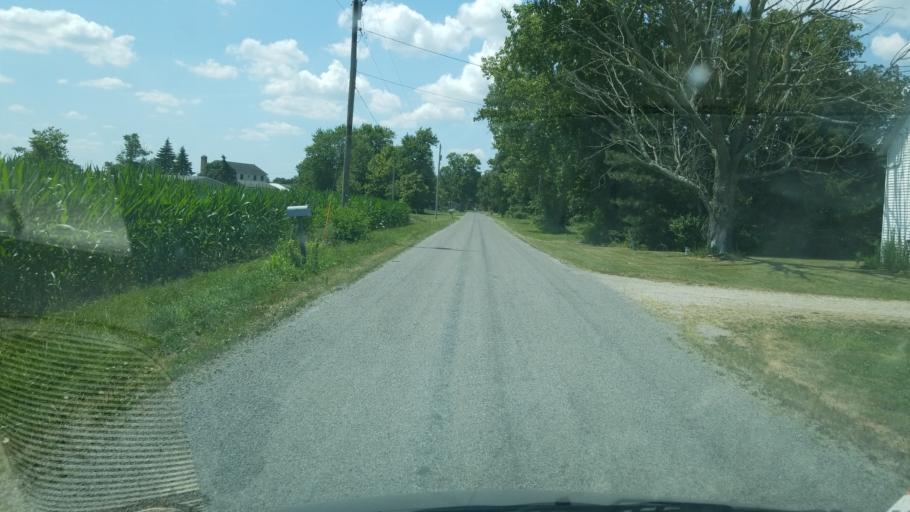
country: US
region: Ohio
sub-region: Champaign County
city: Mechanicsburg
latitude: 40.0783
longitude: -83.4490
